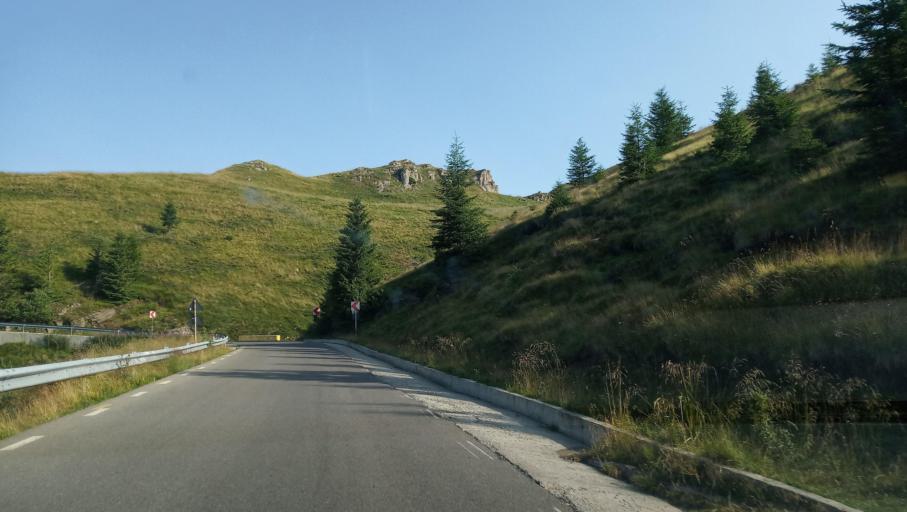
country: RO
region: Prahova
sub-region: Oras Sinaia
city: Sinaia
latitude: 45.3275
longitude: 25.4667
